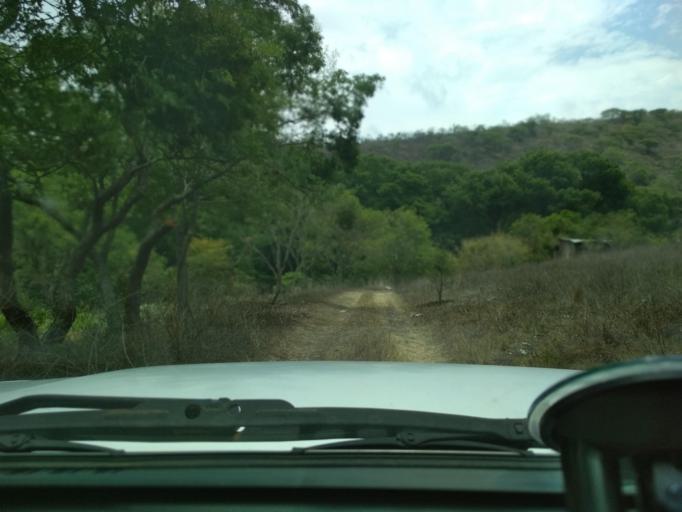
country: MX
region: Veracruz
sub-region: Nogales
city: Taza de Agua Ojo Zarco
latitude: 18.7750
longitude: -97.2052
